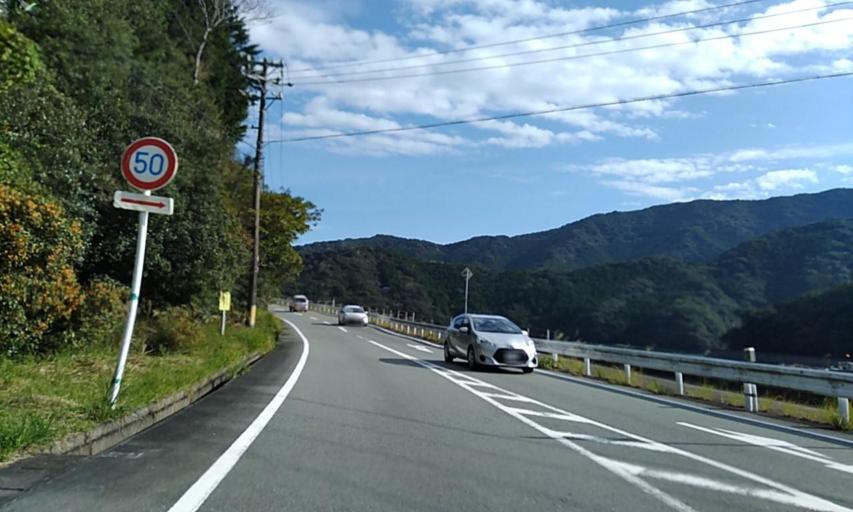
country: JP
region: Mie
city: Owase
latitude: 34.2489
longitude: 136.4404
